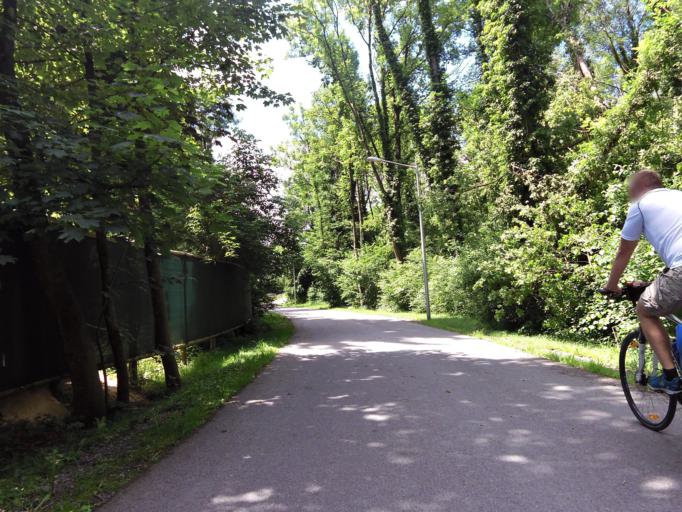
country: AT
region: Vorarlberg
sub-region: Politischer Bezirk Bregenz
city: Hard
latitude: 47.5002
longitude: 9.7040
